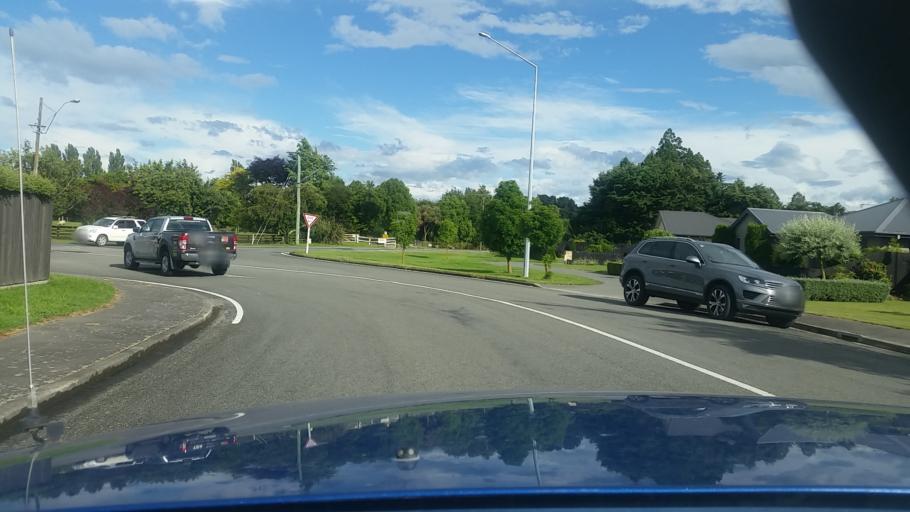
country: NZ
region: Canterbury
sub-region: Ashburton District
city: Ashburton
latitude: -43.8813
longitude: 171.7323
